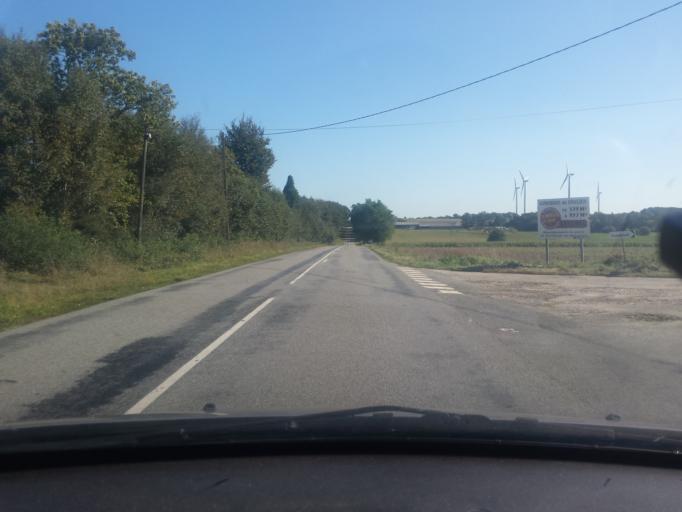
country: FR
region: Brittany
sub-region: Departement du Morbihan
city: Cleguerec
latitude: 48.1131
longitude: -3.1184
